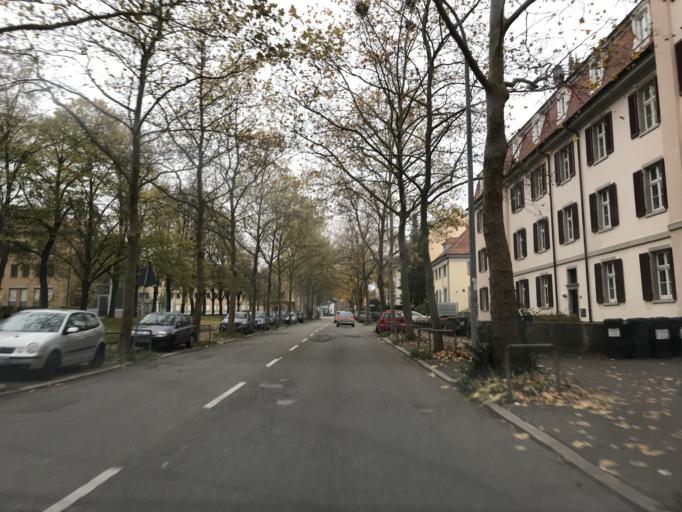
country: DE
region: Baden-Wuerttemberg
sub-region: Freiburg Region
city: Freiburg
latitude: 48.0067
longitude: 7.8508
